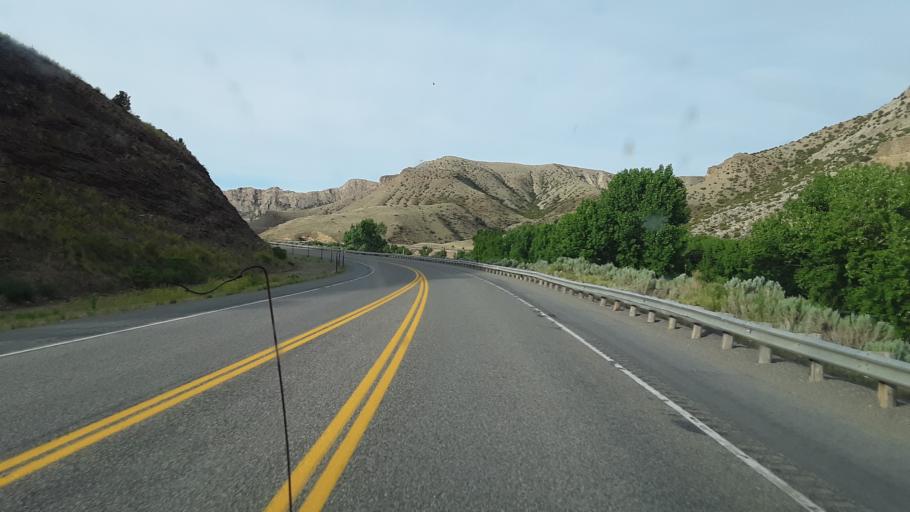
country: US
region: Wyoming
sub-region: Hot Springs County
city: Thermopolis
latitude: 43.4325
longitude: -108.1778
